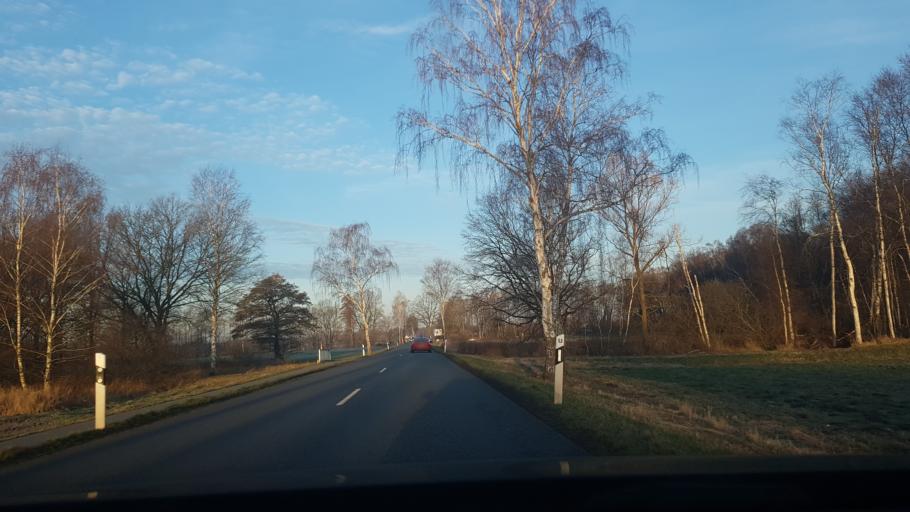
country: DE
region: Lower Saxony
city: Sassenburg
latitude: 52.5046
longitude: 10.6048
